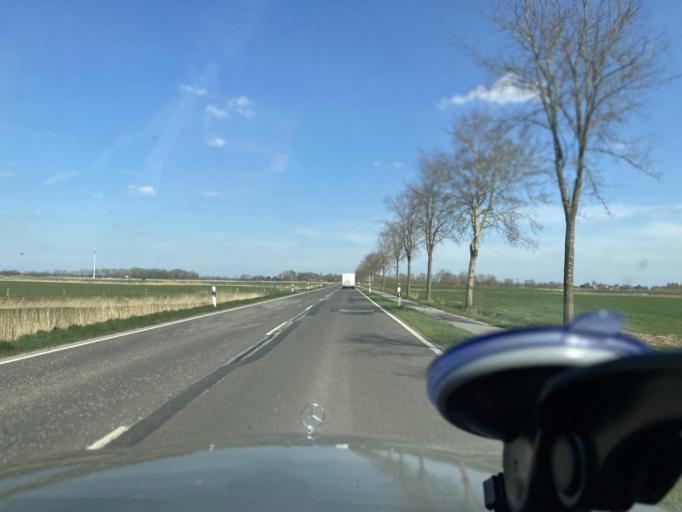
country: DE
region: Schleswig-Holstein
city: Sankt Annen
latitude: 54.3478
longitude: 9.0559
